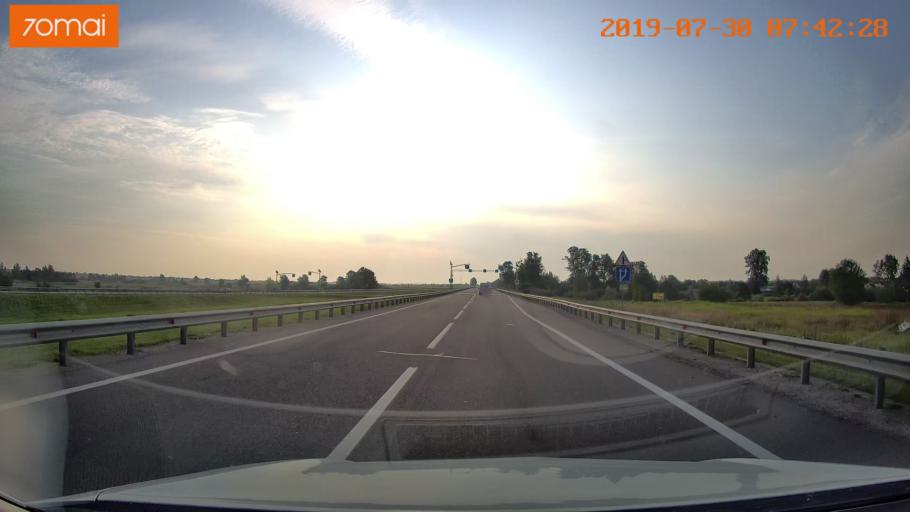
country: RU
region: Kaliningrad
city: Gvardeysk
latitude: 54.6478
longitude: 21.2801
